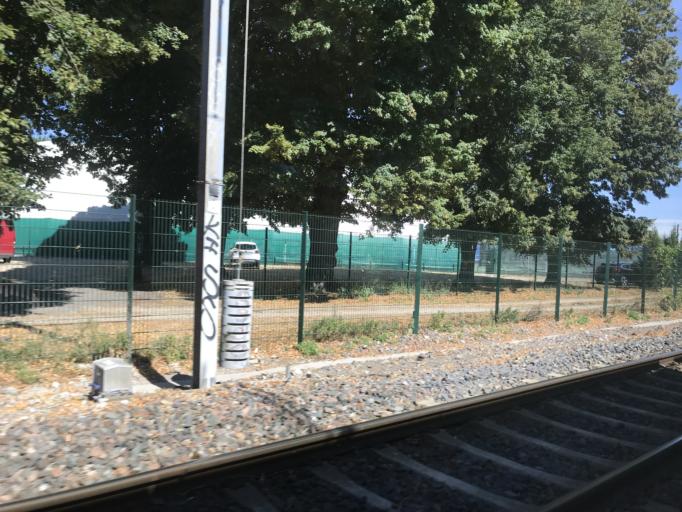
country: FR
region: Champagne-Ardenne
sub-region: Departement de la Marne
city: Reims
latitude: 49.2546
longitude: 4.0181
